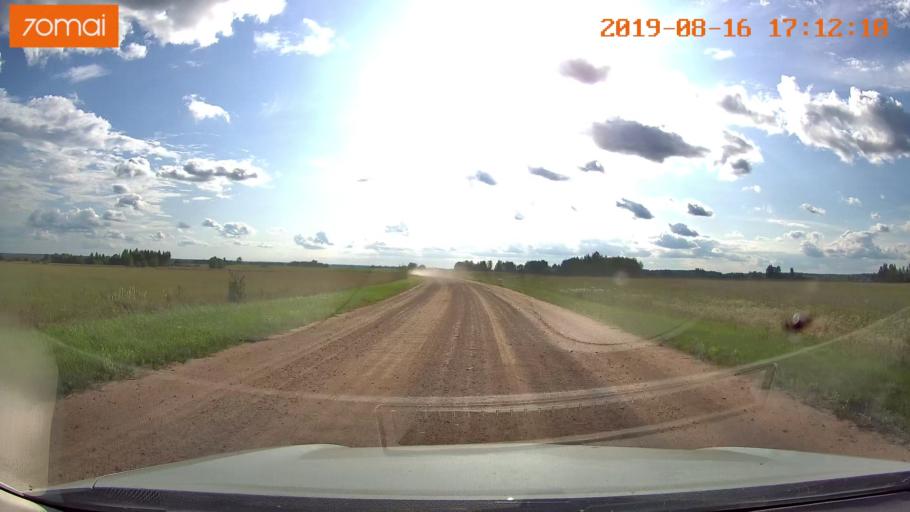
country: BY
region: Mogilev
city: Hlusha
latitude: 53.1962
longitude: 28.8953
